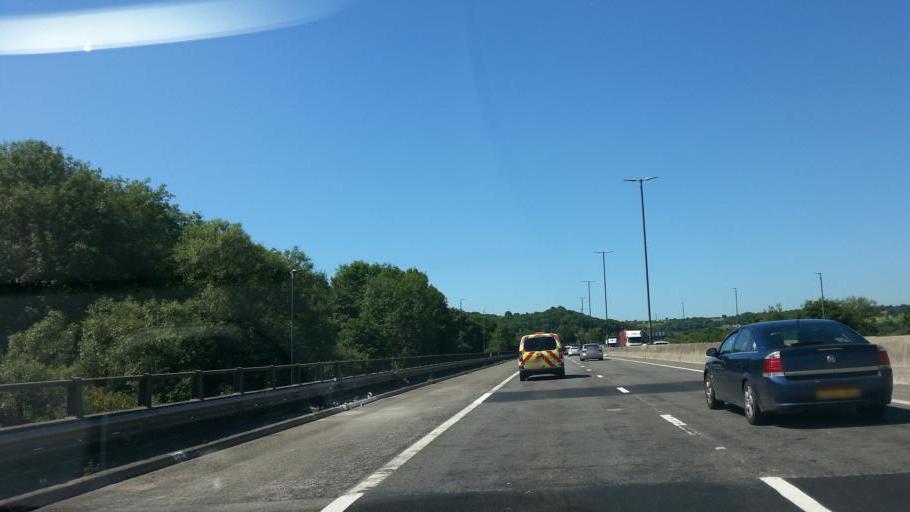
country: GB
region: Wales
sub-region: Newport
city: Newport
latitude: 51.6007
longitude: -3.0052
